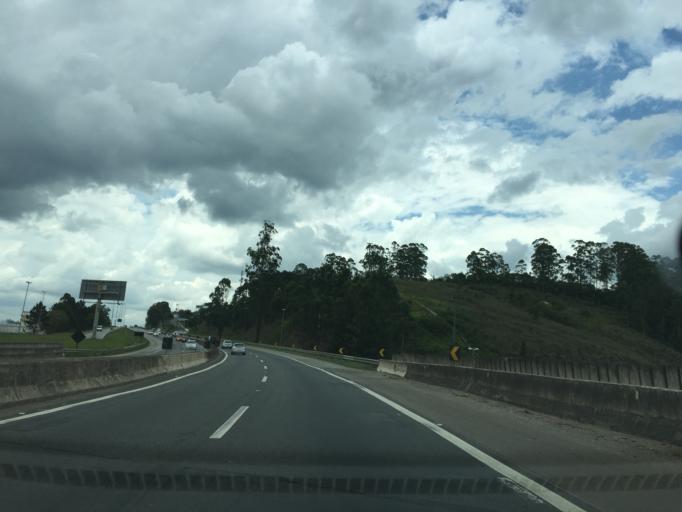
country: BR
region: Sao Paulo
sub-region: Mairipora
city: Mairipora
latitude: -23.2651
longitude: -46.5841
